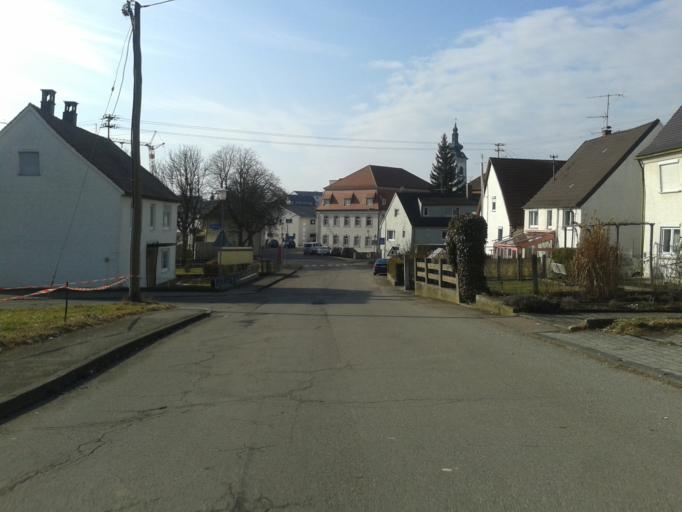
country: DE
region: Baden-Wuerttemberg
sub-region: Tuebingen Region
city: Oberdischingen
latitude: 48.3028
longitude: 9.8350
